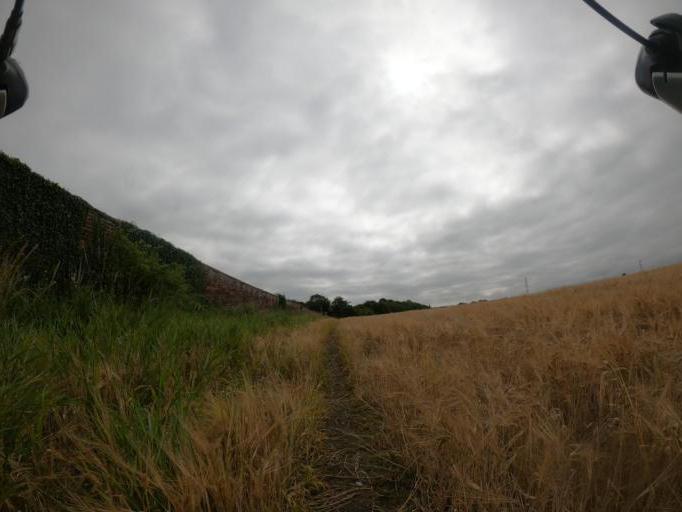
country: GB
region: Scotland
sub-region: East Lothian
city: Musselburgh
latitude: 55.9412
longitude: -3.0817
